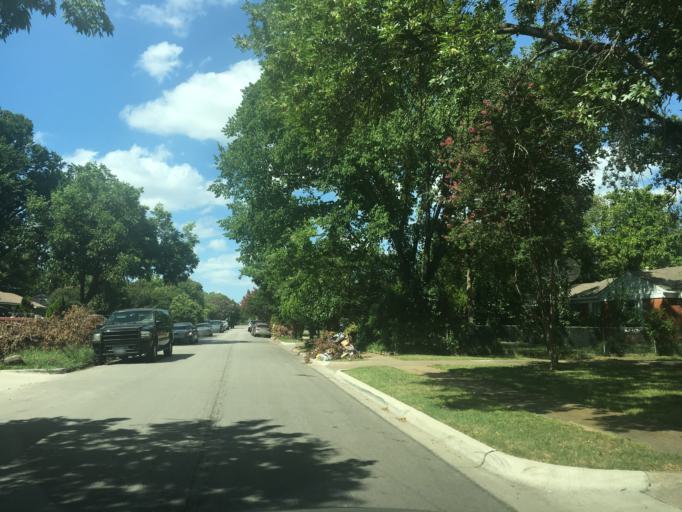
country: US
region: Texas
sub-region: Dallas County
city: Garland
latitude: 32.8375
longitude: -96.6850
